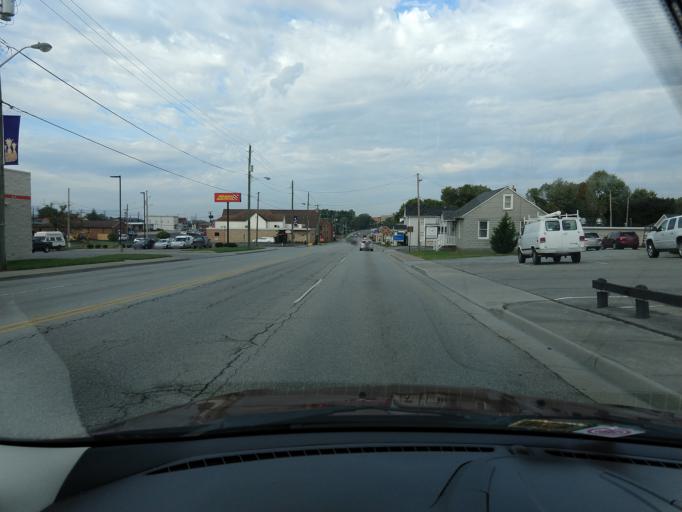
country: US
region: Virginia
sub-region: Roanoke County
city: Vinton
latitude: 37.2814
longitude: -79.8968
